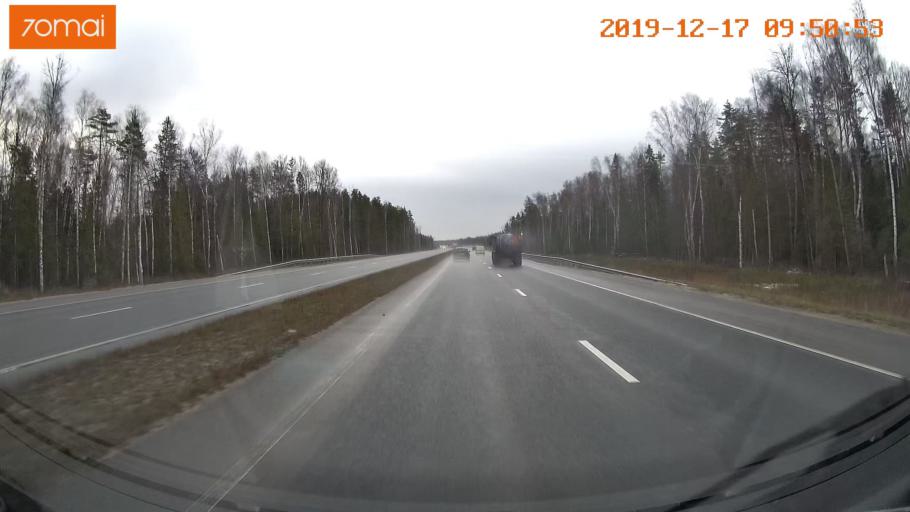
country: RU
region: Vladimir
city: Kommunar
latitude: 56.0521
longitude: 40.5142
